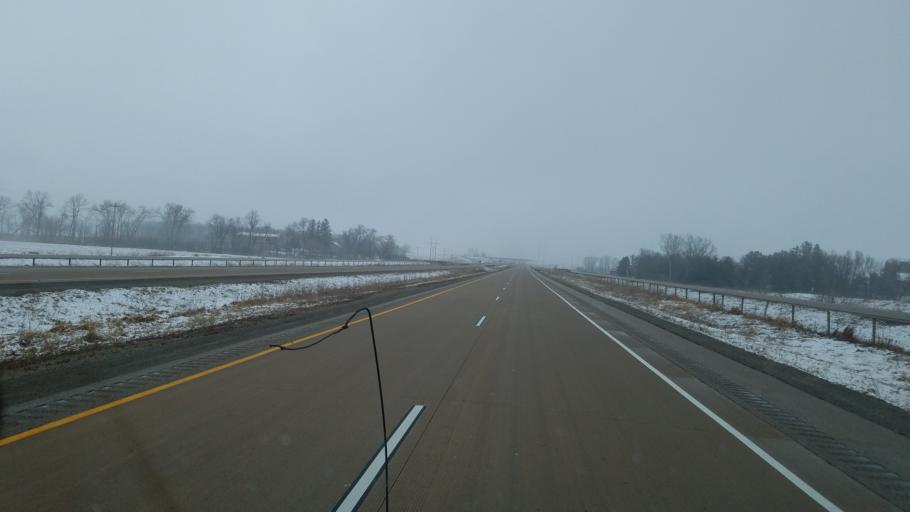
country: US
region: Wisconsin
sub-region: Winnebago County
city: Winneconne
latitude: 44.1599
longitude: -88.6642
